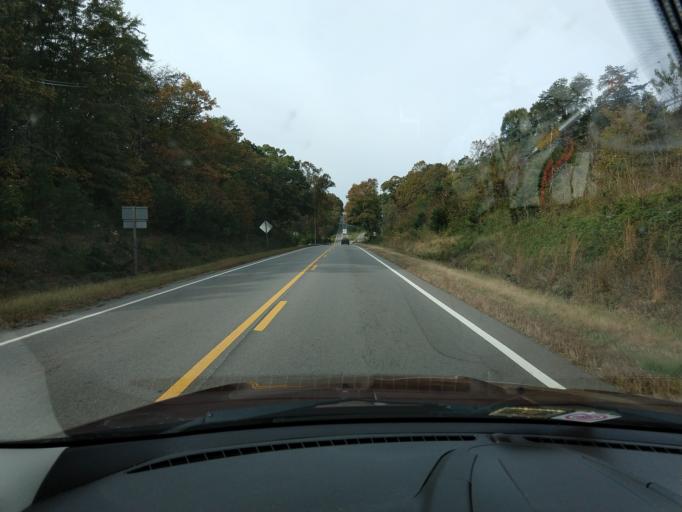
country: US
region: Virginia
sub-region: Pittsylvania County
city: Gretna
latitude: 36.9540
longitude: -79.3846
